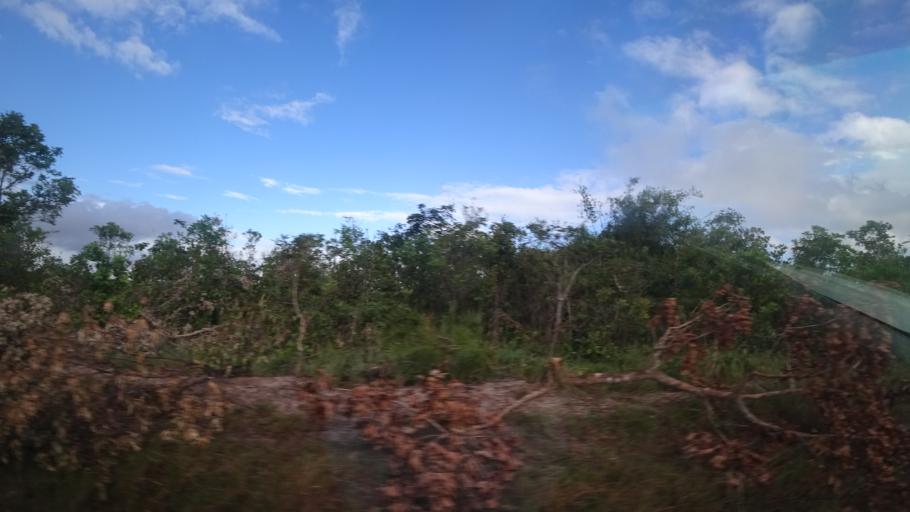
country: MZ
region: Sofala
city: Beira
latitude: -19.6681
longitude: 35.0583
